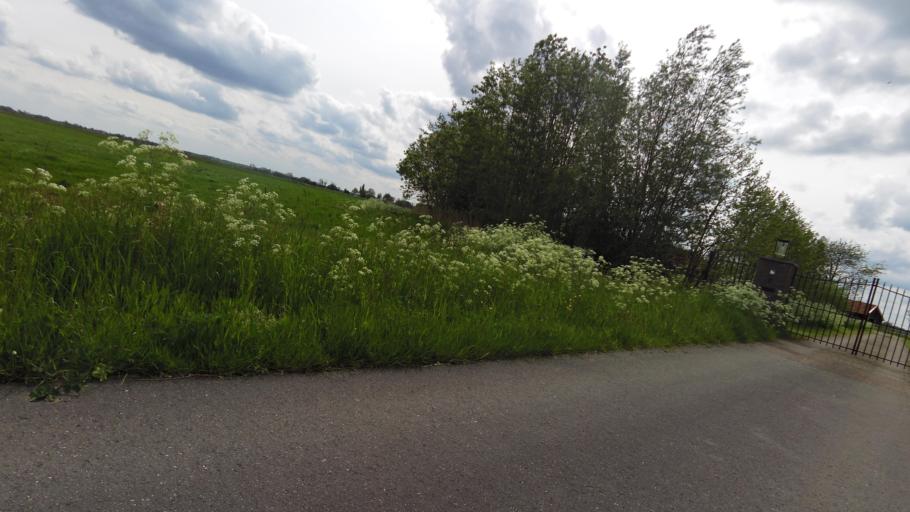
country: NL
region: Utrecht
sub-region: Gemeente Bunschoten
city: Bunschoten
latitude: 52.2441
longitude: 5.4058
